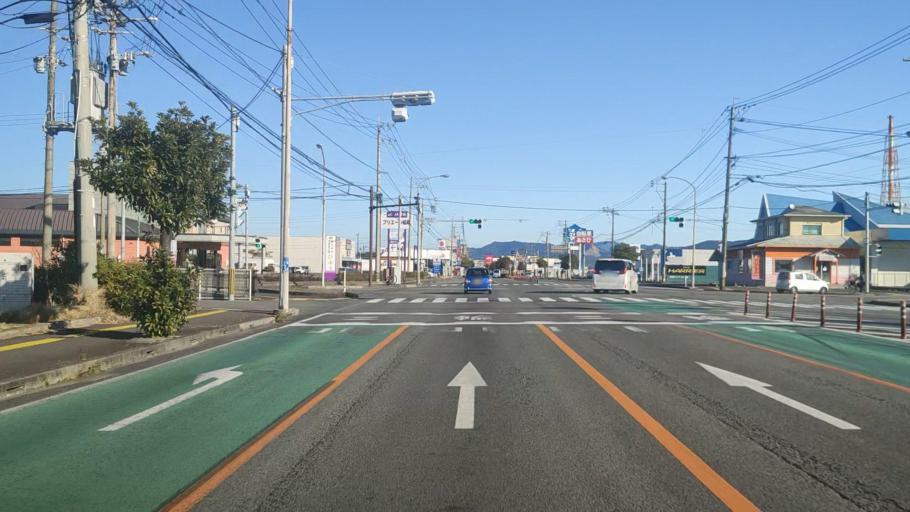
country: JP
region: Miyazaki
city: Nobeoka
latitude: 32.5623
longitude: 131.6813
